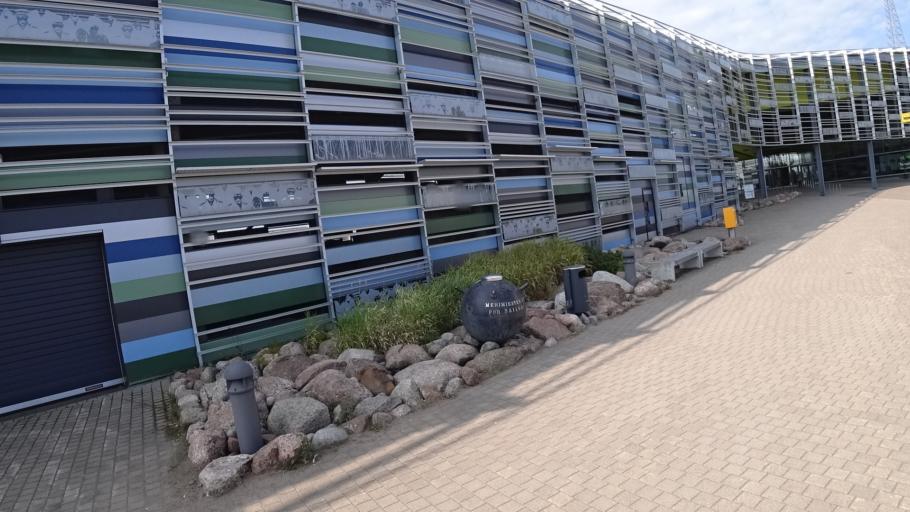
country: FI
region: Kymenlaakso
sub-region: Kotka-Hamina
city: Kotka
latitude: 60.4718
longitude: 26.9445
